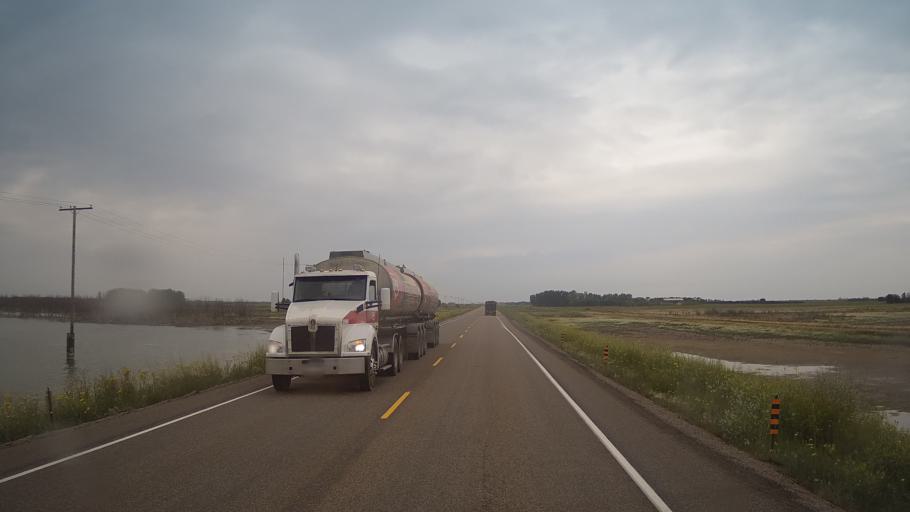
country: CA
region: Saskatchewan
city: Langham
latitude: 52.1289
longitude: -107.1304
